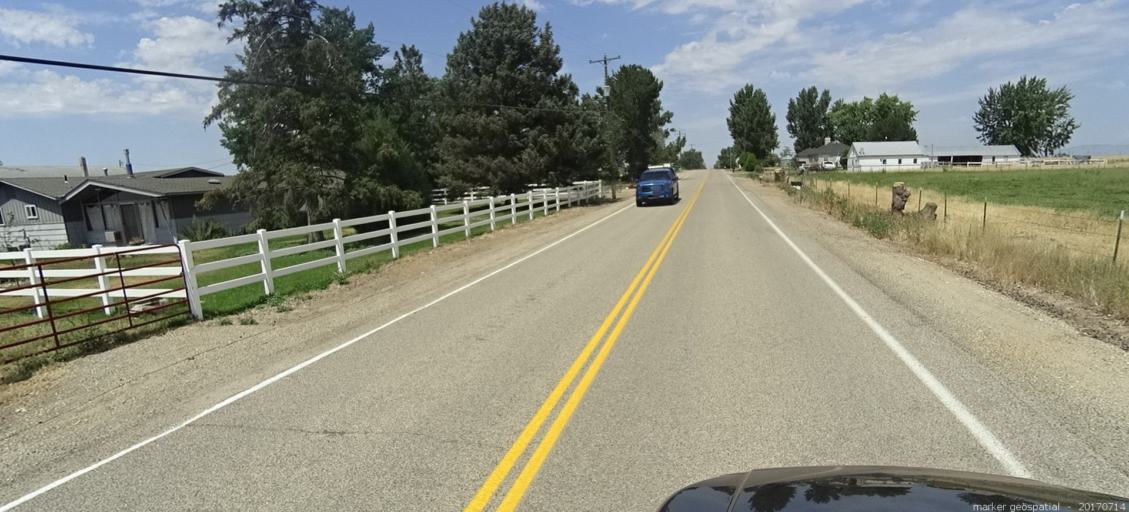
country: US
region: Idaho
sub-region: Ada County
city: Kuna
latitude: 43.5267
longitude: -116.3543
